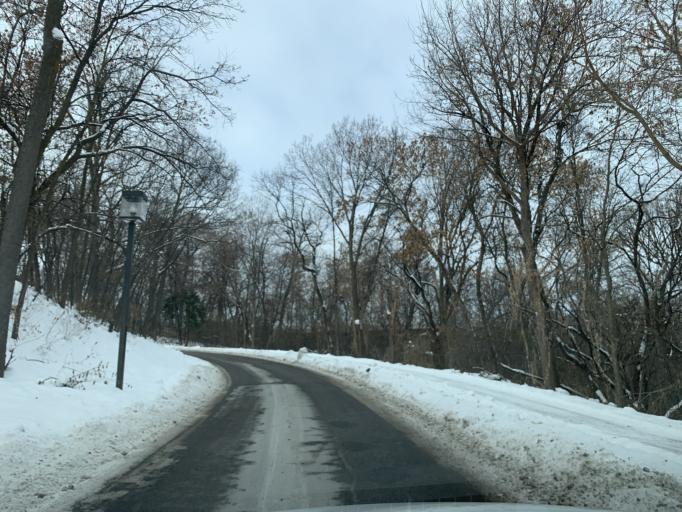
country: US
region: Minnesota
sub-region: Hennepin County
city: Minneapolis
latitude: 44.9691
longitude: -93.2987
